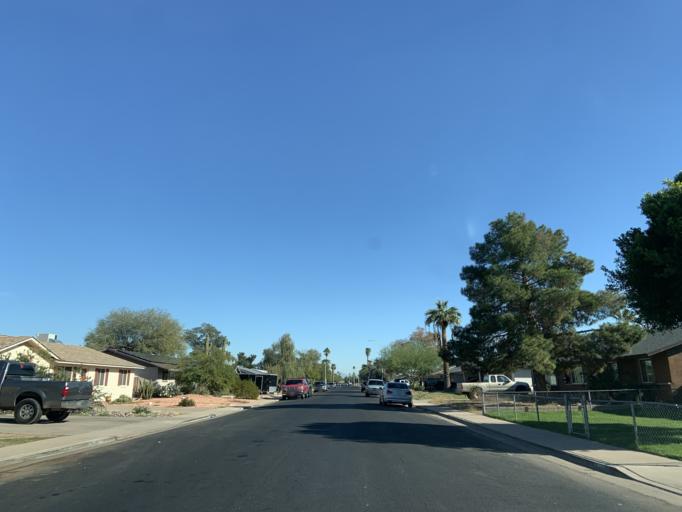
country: US
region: Arizona
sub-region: Maricopa County
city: Tempe
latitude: 33.4050
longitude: -111.8692
